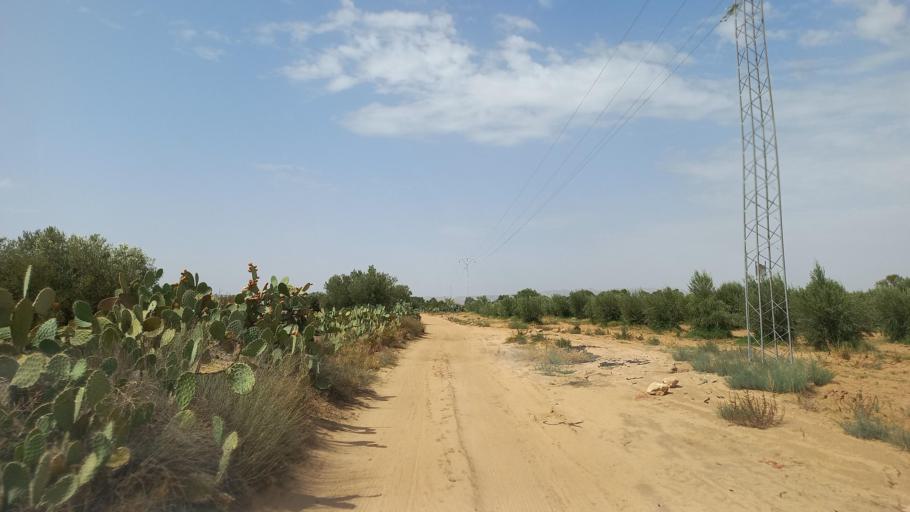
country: TN
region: Al Qasrayn
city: Kasserine
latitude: 35.2582
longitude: 9.0534
